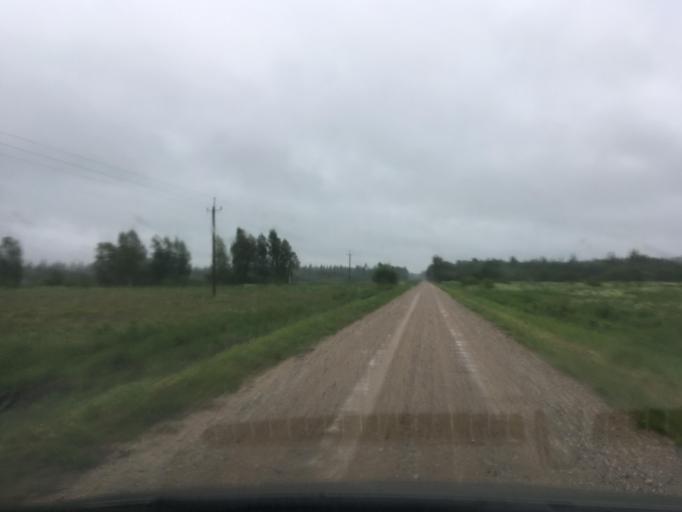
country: EE
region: Laeaene
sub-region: Lihula vald
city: Lihula
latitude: 58.6046
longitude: 23.8321
